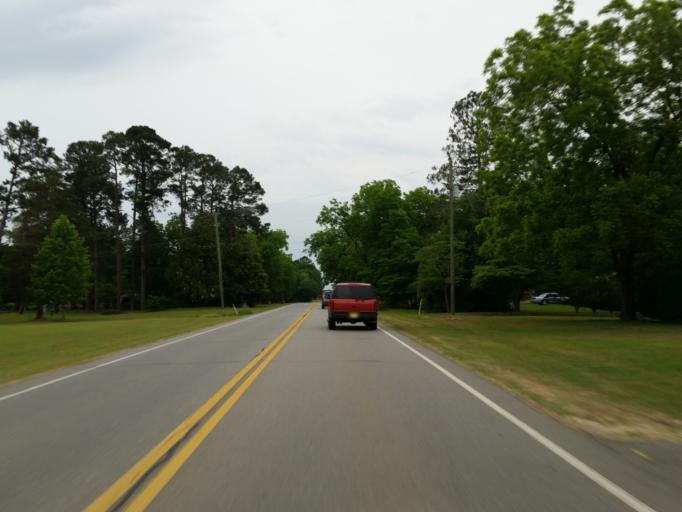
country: US
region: Georgia
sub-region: Dooly County
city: Vienna
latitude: 32.1201
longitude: -83.7982
